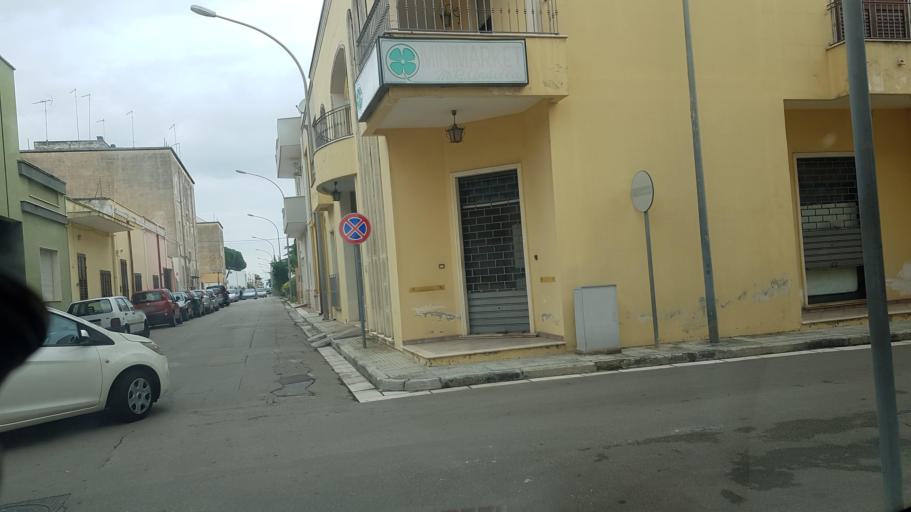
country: IT
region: Apulia
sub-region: Provincia di Lecce
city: Squinzano
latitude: 40.4317
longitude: 18.0373
